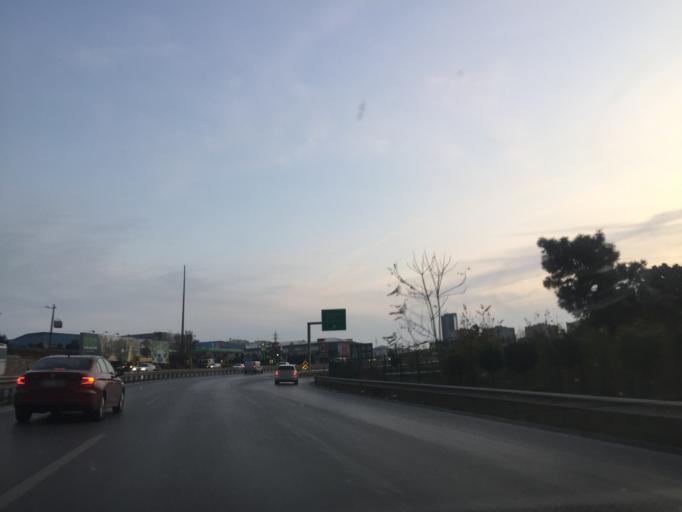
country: TR
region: Istanbul
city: Samandira
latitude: 40.9715
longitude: 29.2196
